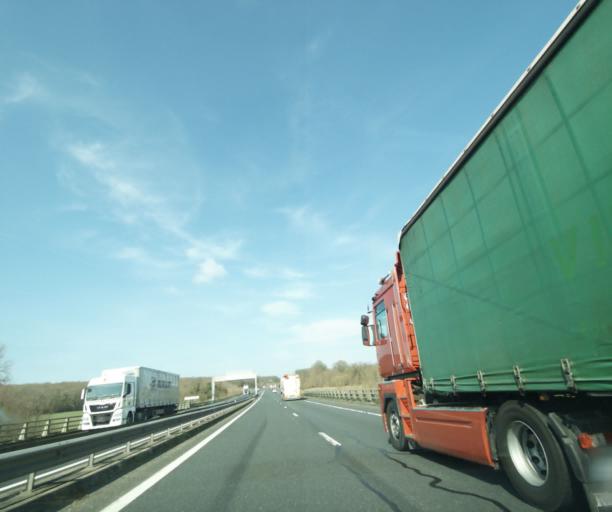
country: FR
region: Centre
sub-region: Departement de l'Indre
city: Saint-Marcel
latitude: 46.6301
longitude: 1.5493
